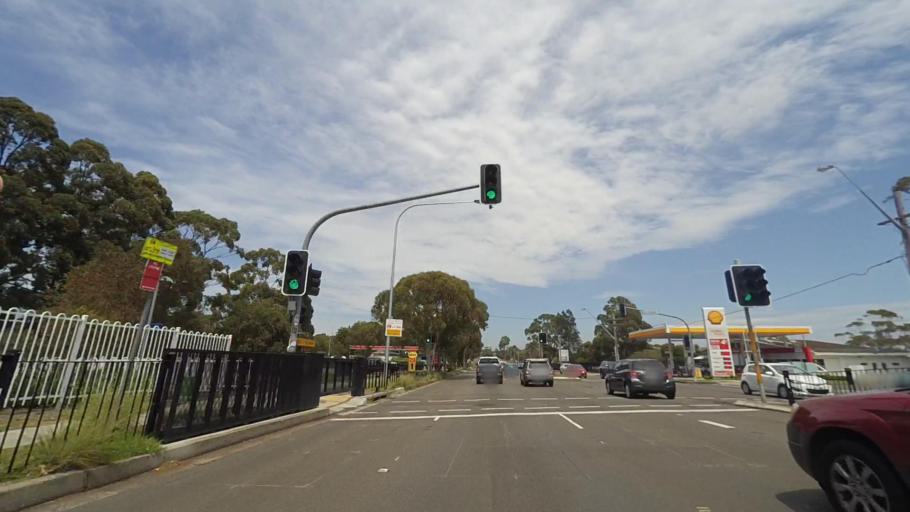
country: AU
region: New South Wales
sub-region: Sutherland Shire
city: Heathcote
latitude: -34.0877
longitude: 151.0077
